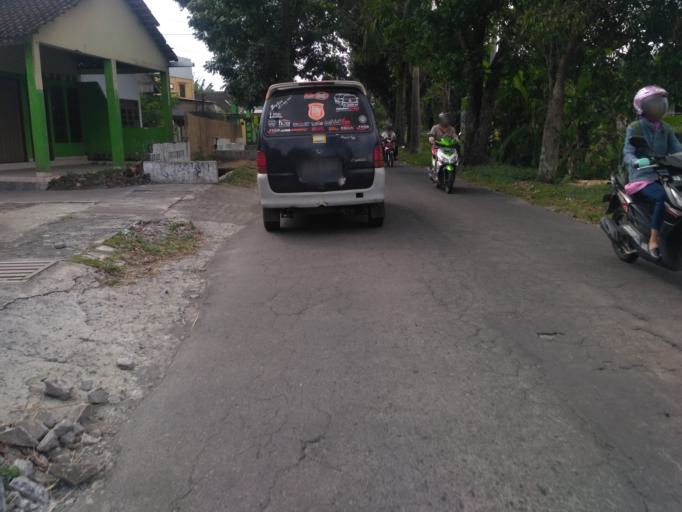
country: ID
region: Daerah Istimewa Yogyakarta
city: Melati
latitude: -7.7295
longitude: 110.3554
